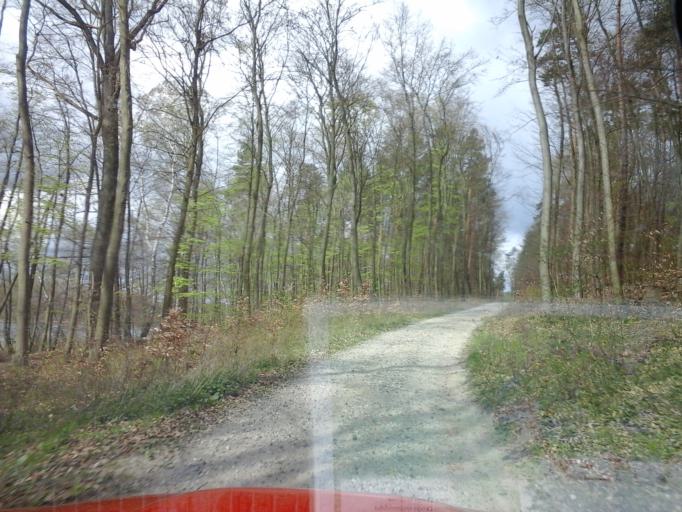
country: PL
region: West Pomeranian Voivodeship
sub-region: Powiat choszczenski
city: Bierzwnik
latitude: 53.0390
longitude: 15.6077
